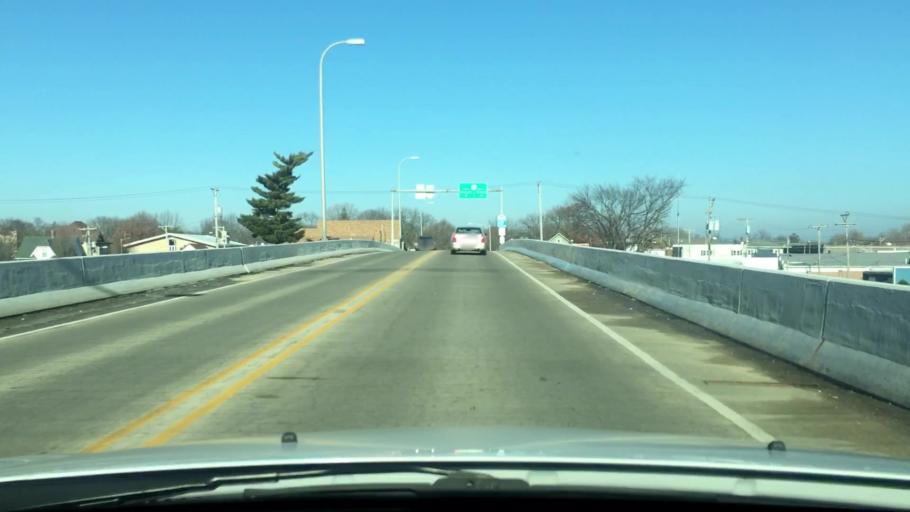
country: US
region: Illinois
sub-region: Ogle County
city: Rochelle
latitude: 41.9208
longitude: -89.0687
